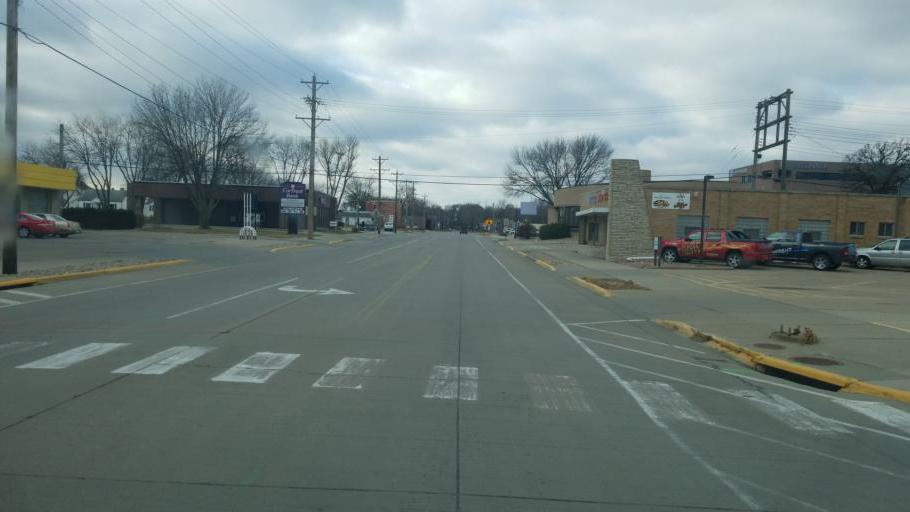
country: US
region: South Dakota
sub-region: Yankton County
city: Yankton
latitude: 42.8686
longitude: -97.3939
